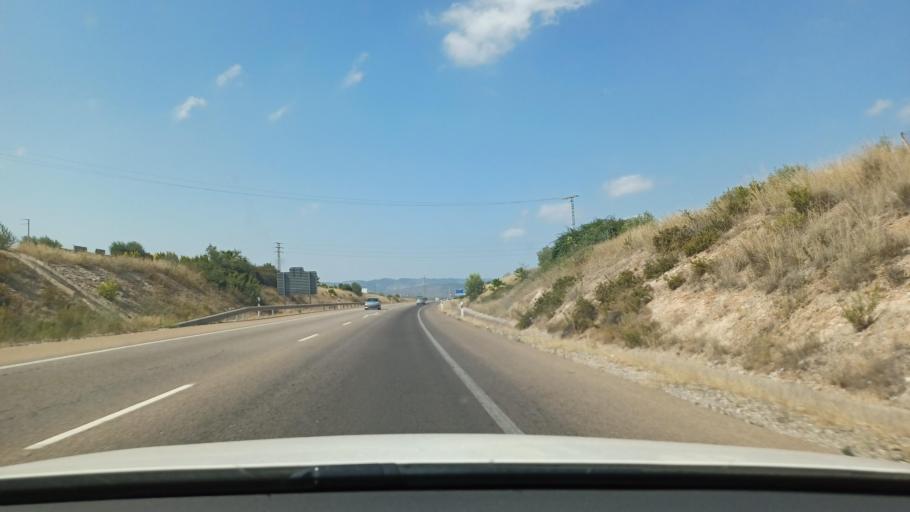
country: ES
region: Valencia
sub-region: Provincia de Castello
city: Vila-real
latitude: 39.9605
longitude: -0.0859
